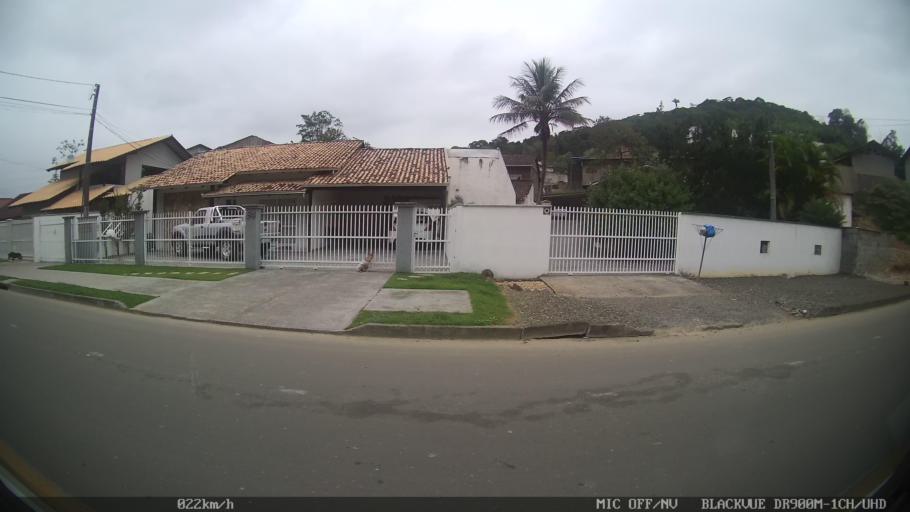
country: BR
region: Santa Catarina
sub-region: Joinville
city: Joinville
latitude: -26.3673
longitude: -48.8343
